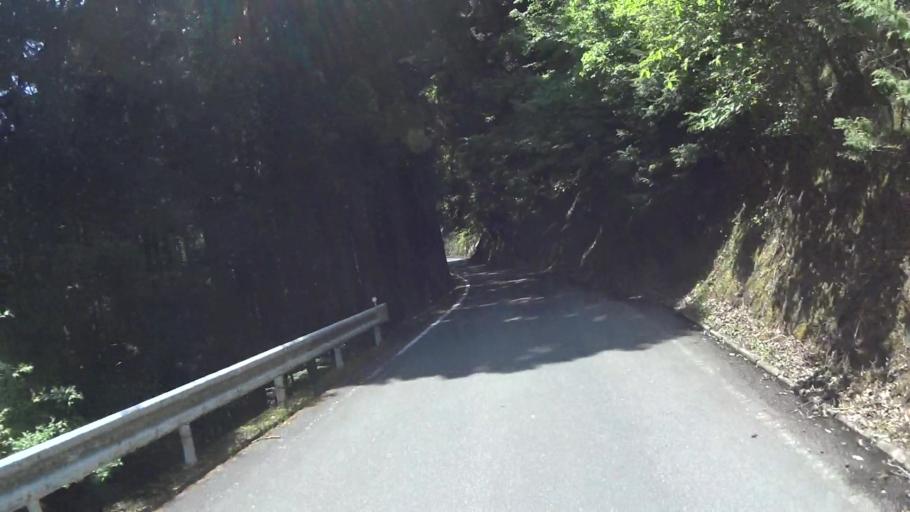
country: JP
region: Kyoto
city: Kameoka
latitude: 35.1273
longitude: 135.5823
